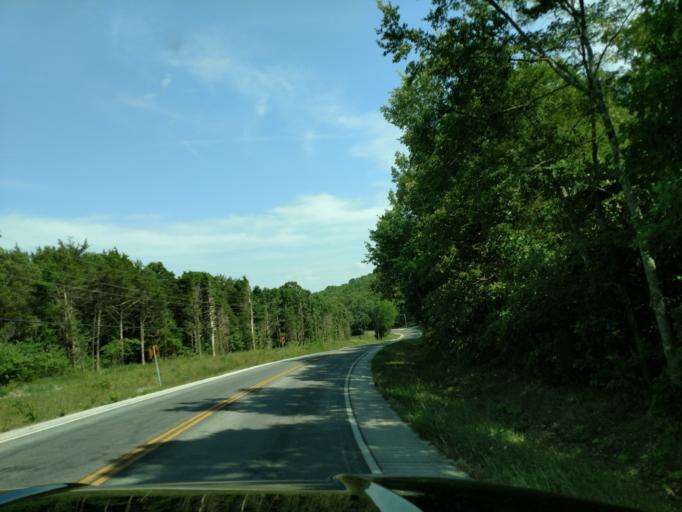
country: US
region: Missouri
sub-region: Barry County
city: Shell Knob
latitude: 36.6124
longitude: -93.5931
